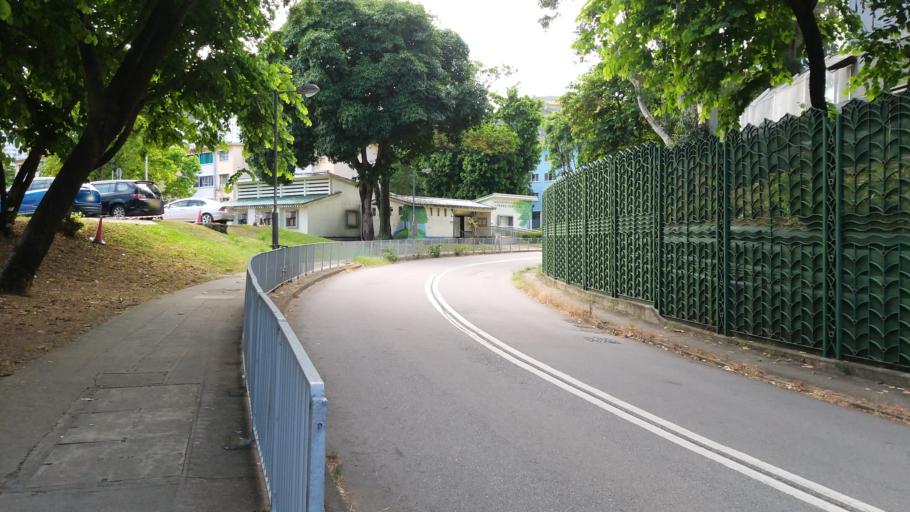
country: HK
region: Tuen Mun
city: Tuen Mun
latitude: 22.4088
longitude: 113.9716
